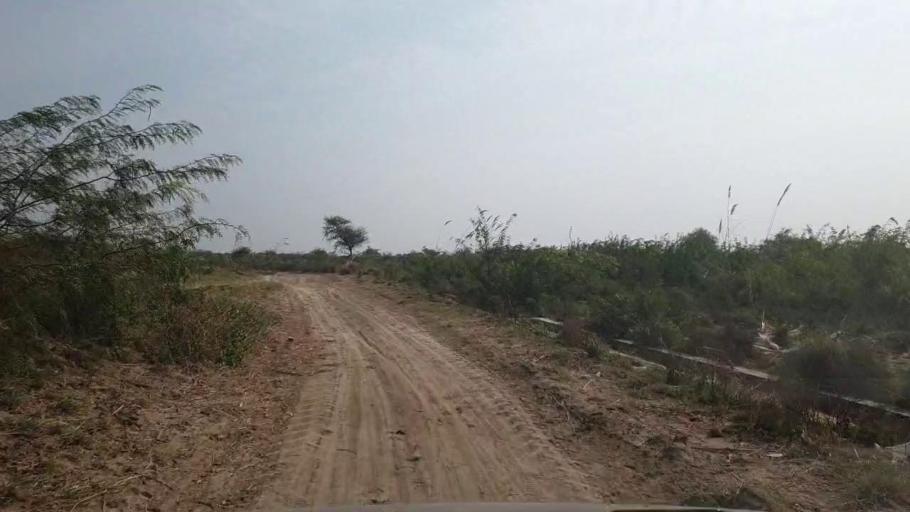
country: PK
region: Sindh
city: Tando Muhammad Khan
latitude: 25.1624
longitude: 68.4717
